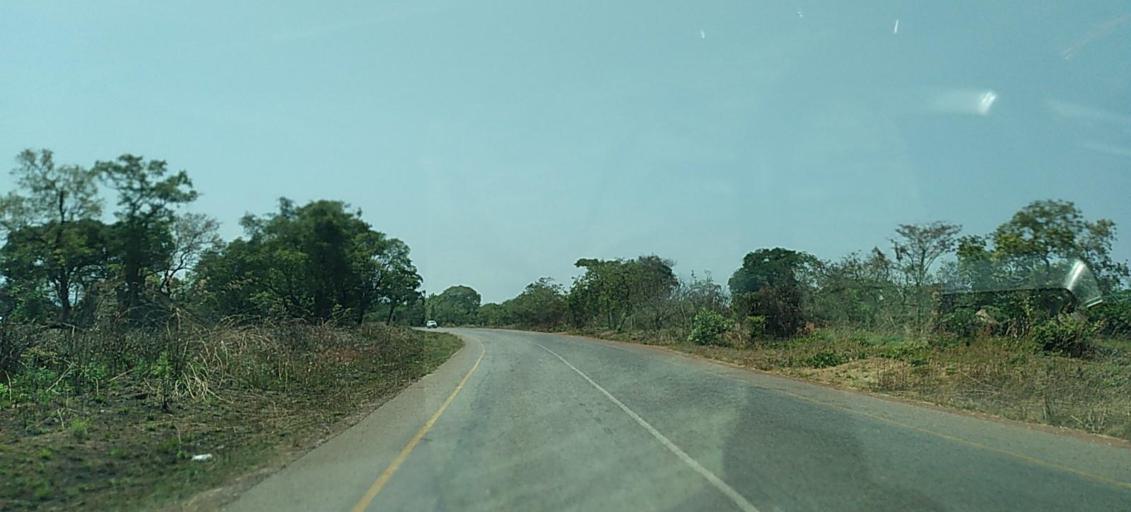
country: ZM
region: North-Western
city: Solwezi
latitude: -12.3916
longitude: 26.2100
